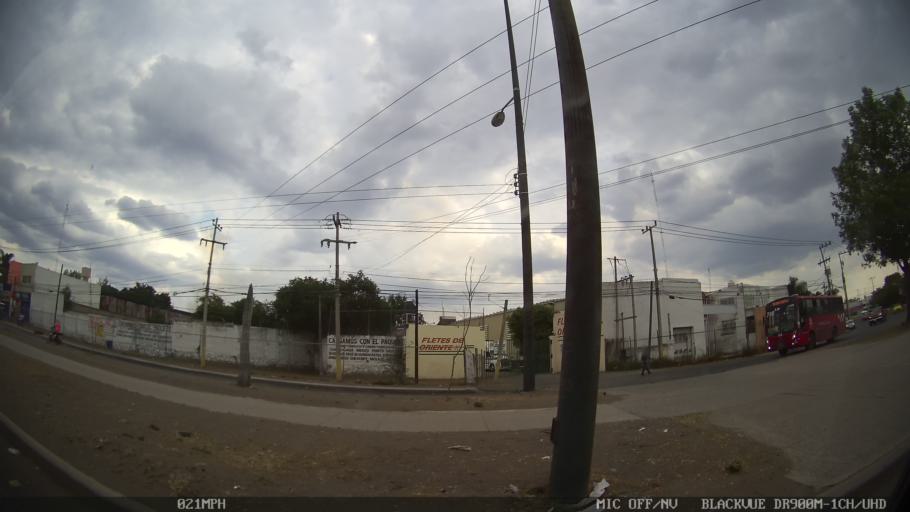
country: MX
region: Jalisco
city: Tlaquepaque
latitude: 20.6164
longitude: -103.2833
